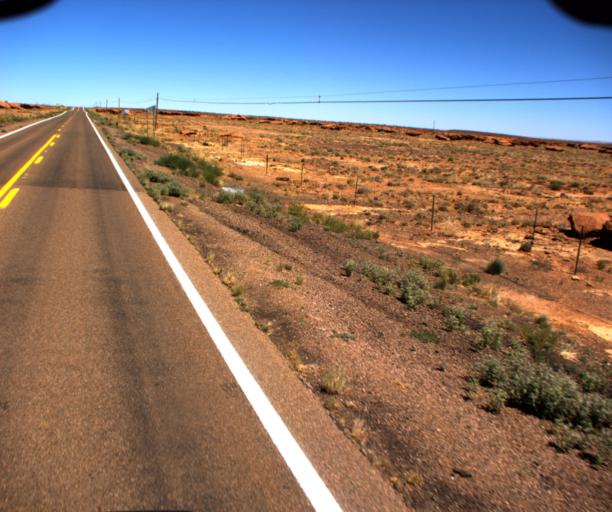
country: US
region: Arizona
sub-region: Navajo County
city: Winslow
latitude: 34.9873
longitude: -110.6644
